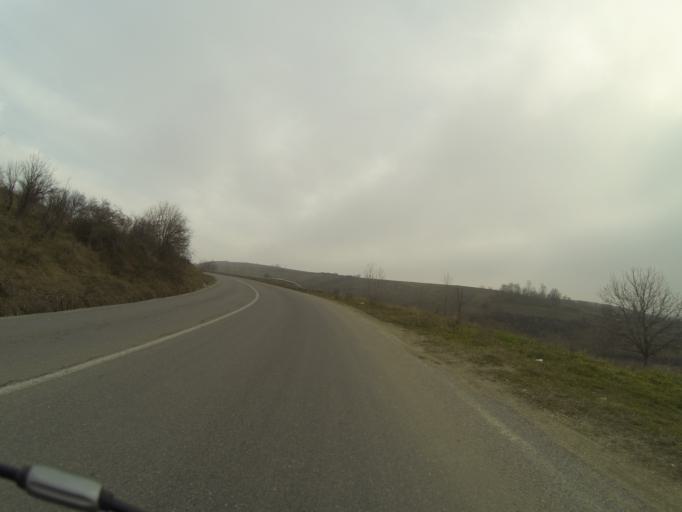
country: RO
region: Mehedinti
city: Vanju-Mare
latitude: 44.4132
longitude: 22.8772
